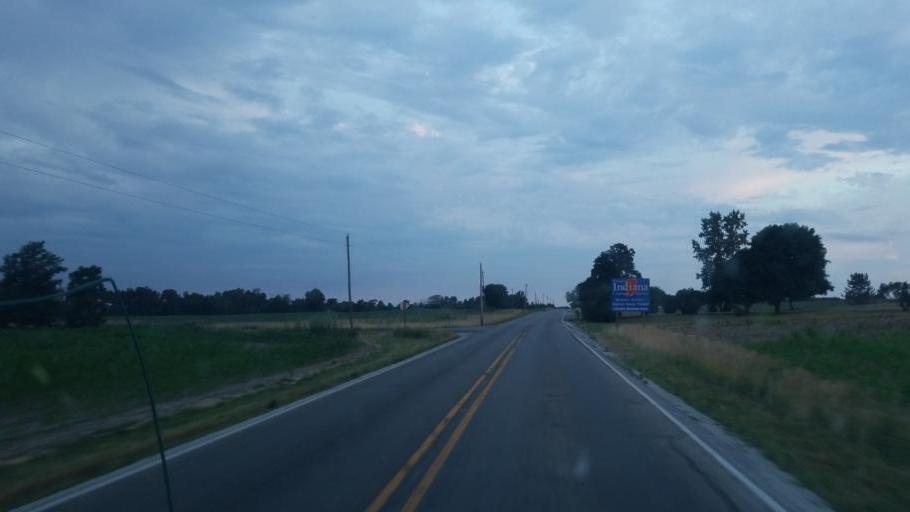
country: US
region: Ohio
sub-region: Defiance County
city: Hicksville
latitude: 41.3287
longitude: -84.8092
